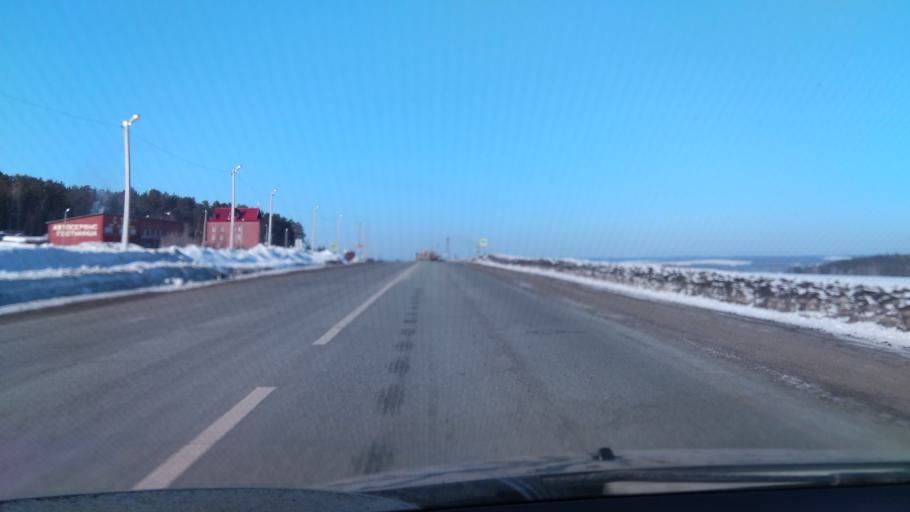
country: RU
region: Sverdlovsk
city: Bisert'
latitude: 56.8330
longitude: 58.8028
